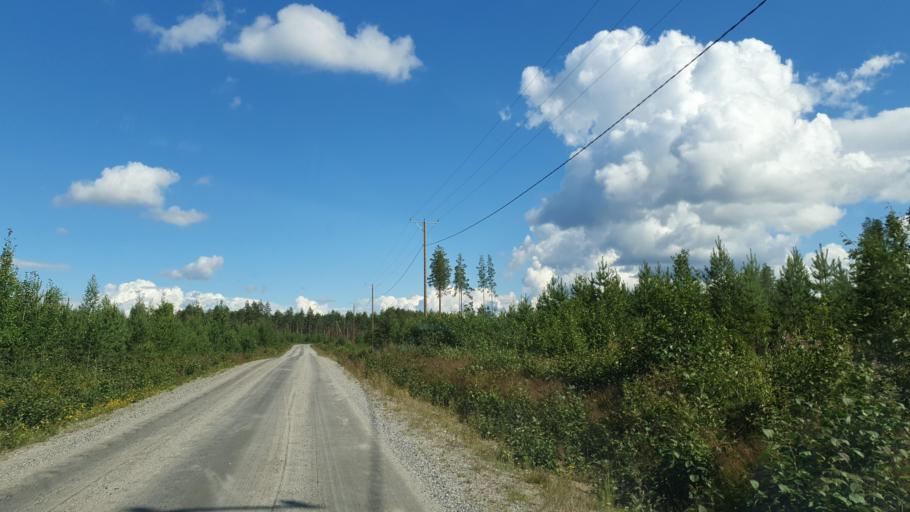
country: FI
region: Kainuu
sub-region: Kehys-Kainuu
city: Kuhmo
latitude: 64.1108
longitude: 29.3698
